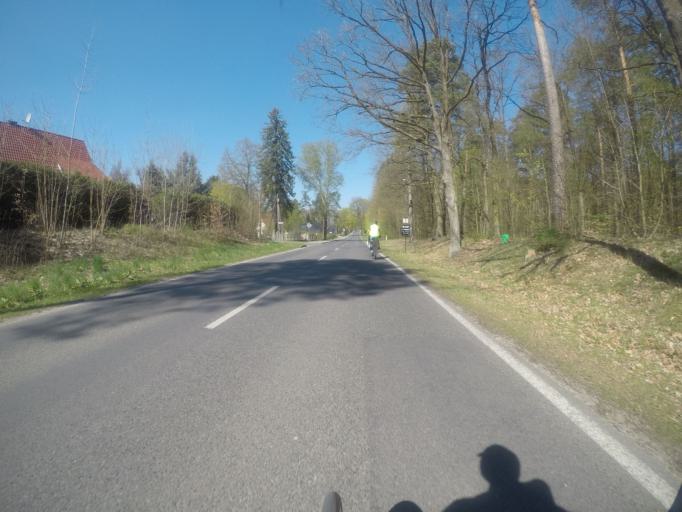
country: DE
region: Brandenburg
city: Rudnitz
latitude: 52.7531
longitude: 13.5660
